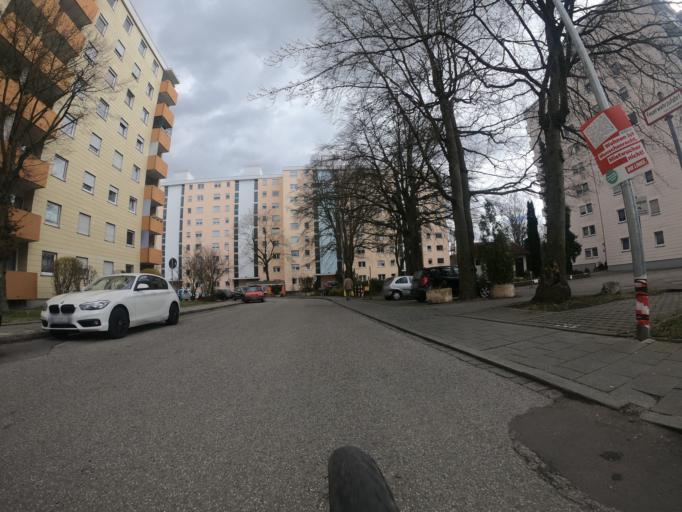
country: DE
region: Bavaria
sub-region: Upper Bavaria
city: Fuerstenfeldbruck
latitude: 48.1632
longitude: 11.2289
